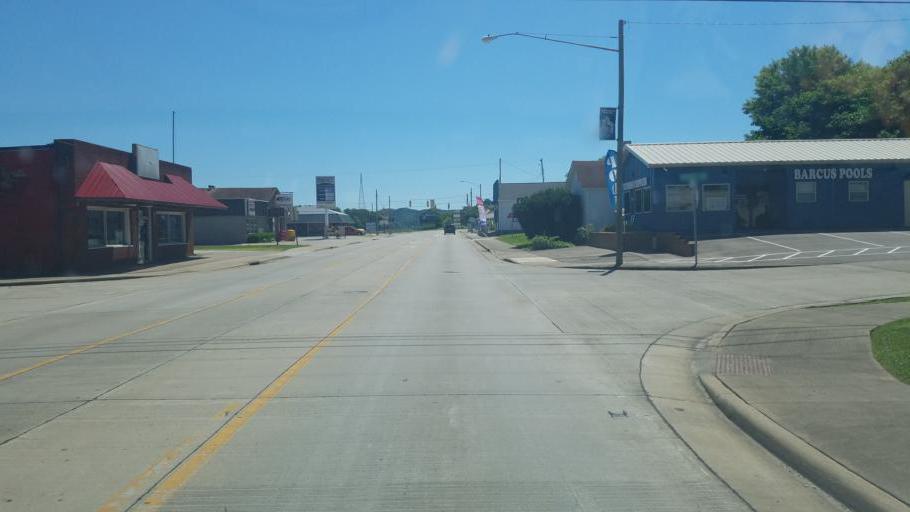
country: US
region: West Virginia
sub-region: Cabell County
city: Pea Ridge
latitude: 38.4380
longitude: -82.3785
